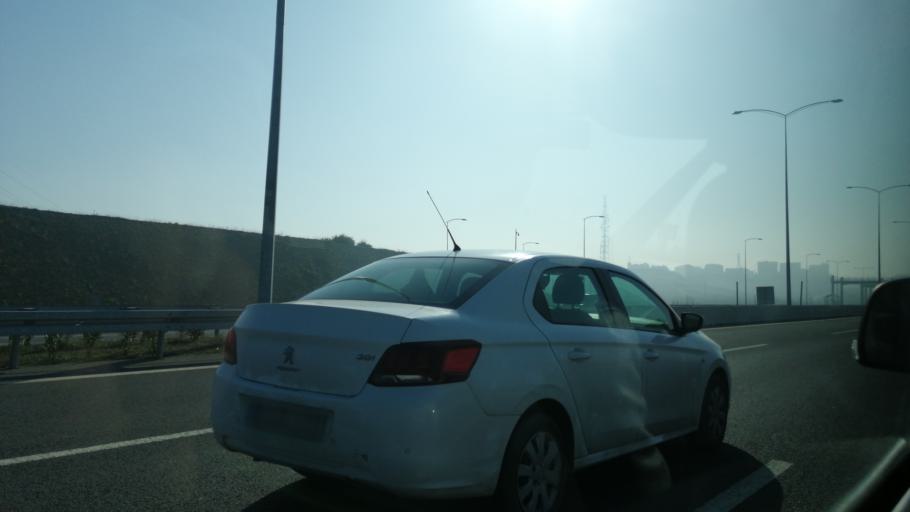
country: TR
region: Kocaeli
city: Tavsanli
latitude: 40.7873
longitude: 29.5148
